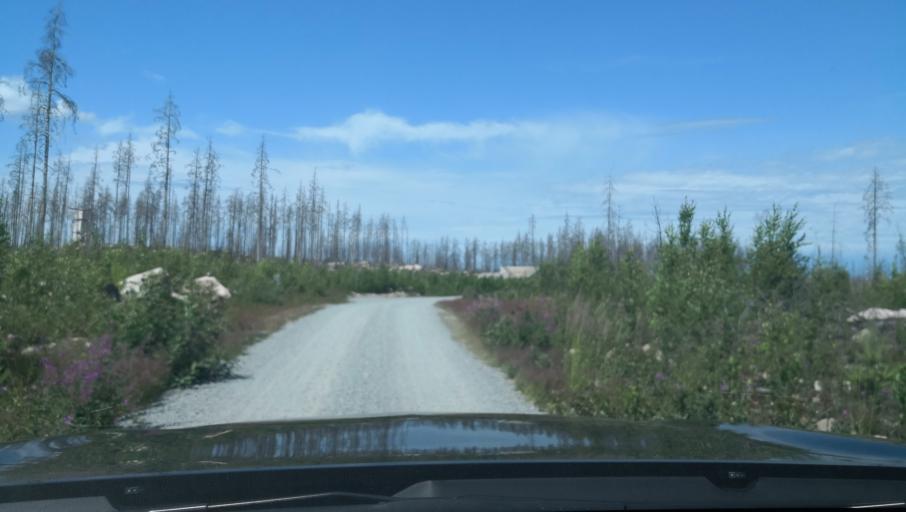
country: SE
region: Vaestmanland
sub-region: Surahammars Kommun
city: Ramnas
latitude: 59.9114
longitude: 16.1493
